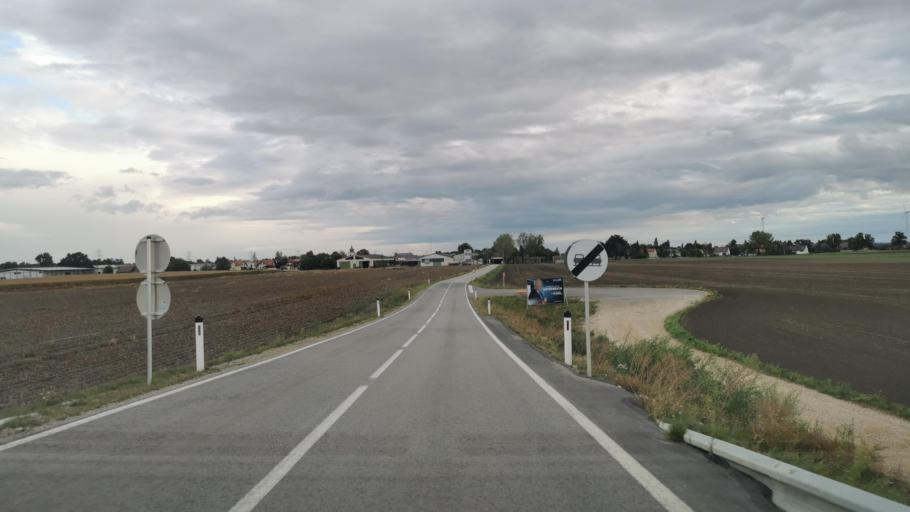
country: AT
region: Lower Austria
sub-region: Politischer Bezirk Ganserndorf
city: Raasdorf
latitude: 48.2395
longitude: 16.5649
